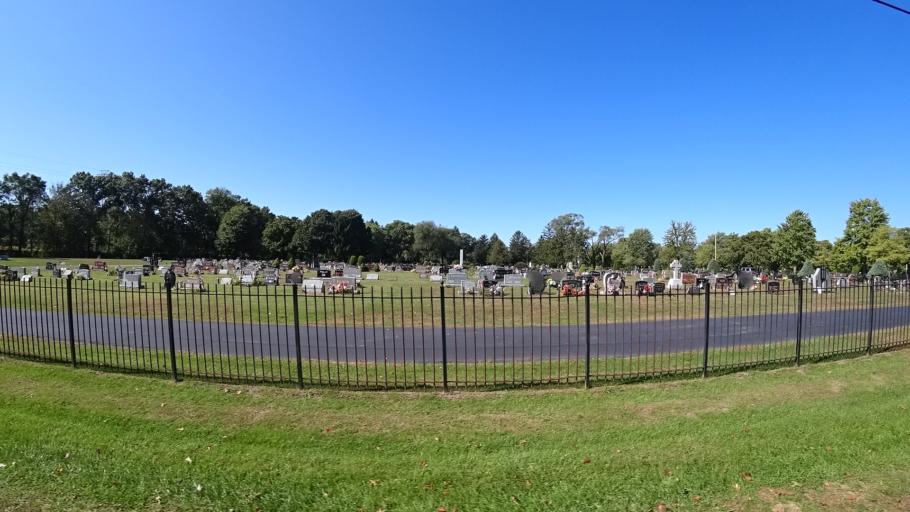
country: US
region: Indiana
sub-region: LaPorte County
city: Michigan City
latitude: 41.7017
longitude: -86.8794
